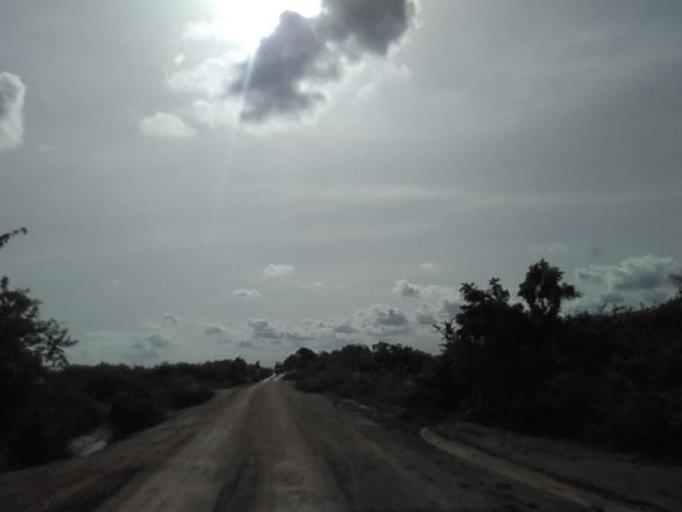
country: GH
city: Akropong
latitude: 6.0339
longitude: 0.3204
